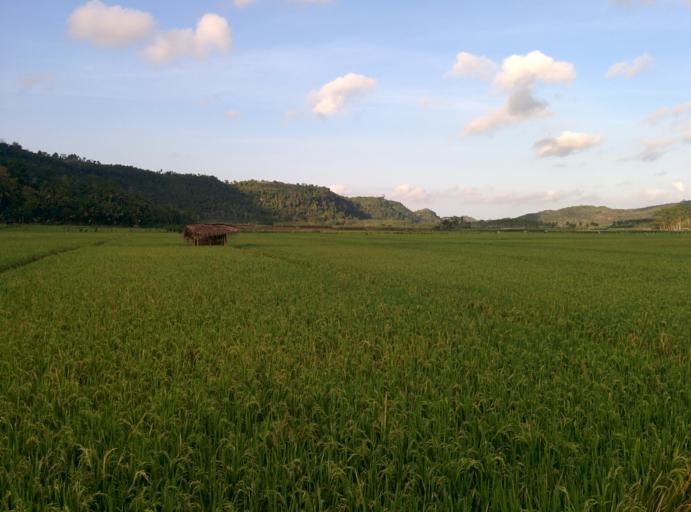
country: ID
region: East Java
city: Sitiarjo
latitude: -8.3845
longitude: 112.6775
